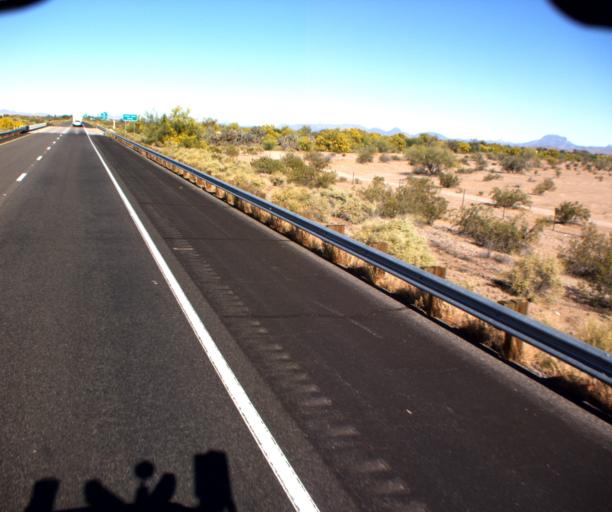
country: US
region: Arizona
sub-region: Maricopa County
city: Gila Bend
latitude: 32.9326
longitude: -112.7040
